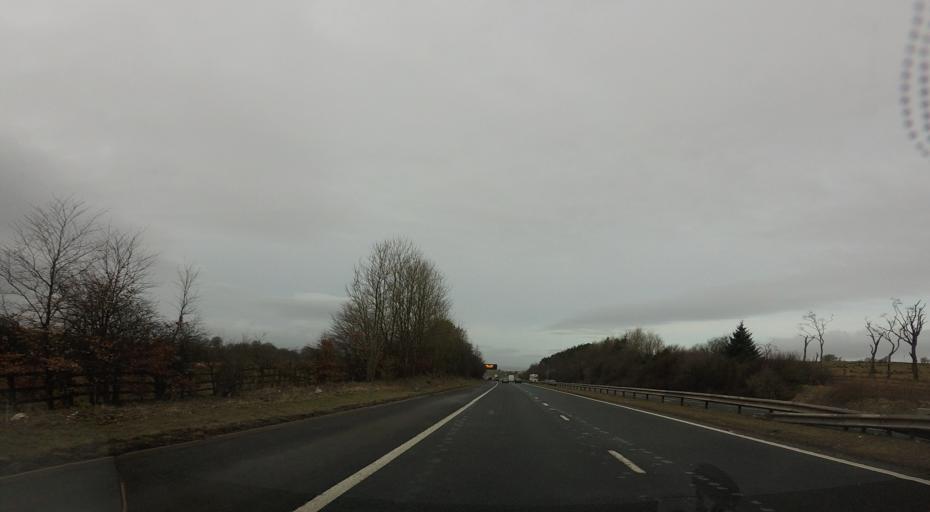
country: GB
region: Scotland
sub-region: North Lanarkshire
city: Cleland
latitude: 55.8431
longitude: -3.8987
